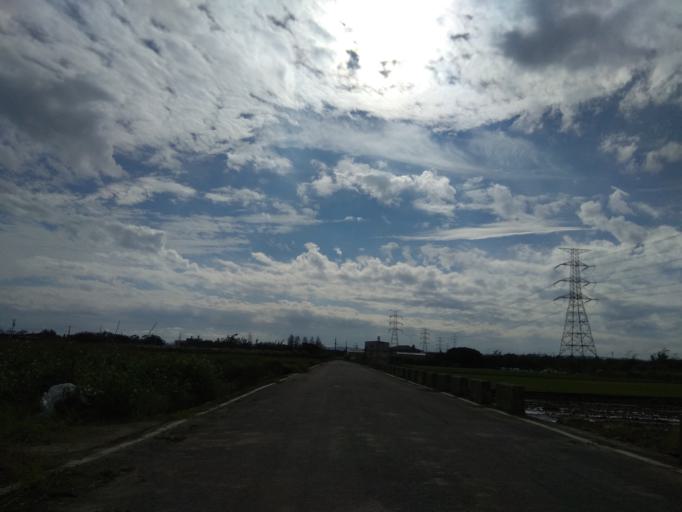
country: TW
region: Taiwan
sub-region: Hsinchu
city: Zhubei
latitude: 24.9503
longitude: 121.1054
